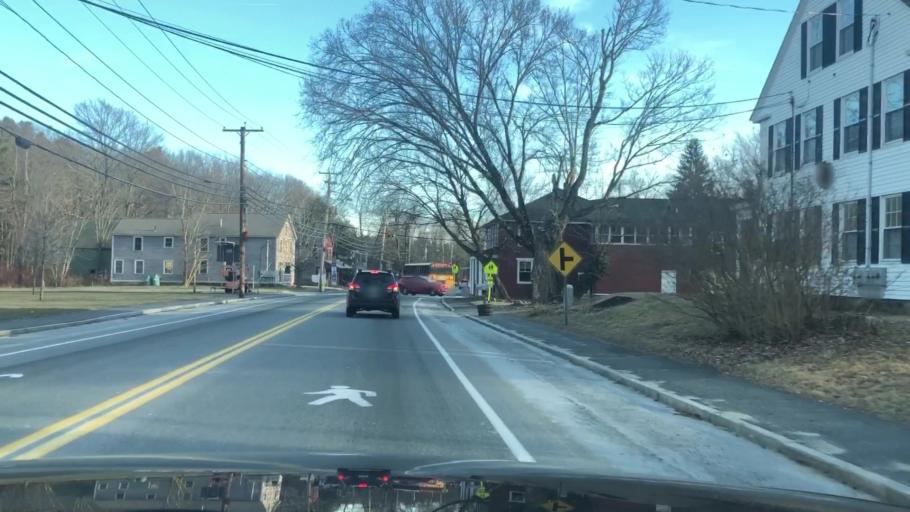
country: US
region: Massachusetts
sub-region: Worcester County
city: Bolton
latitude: 42.4344
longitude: -71.6104
